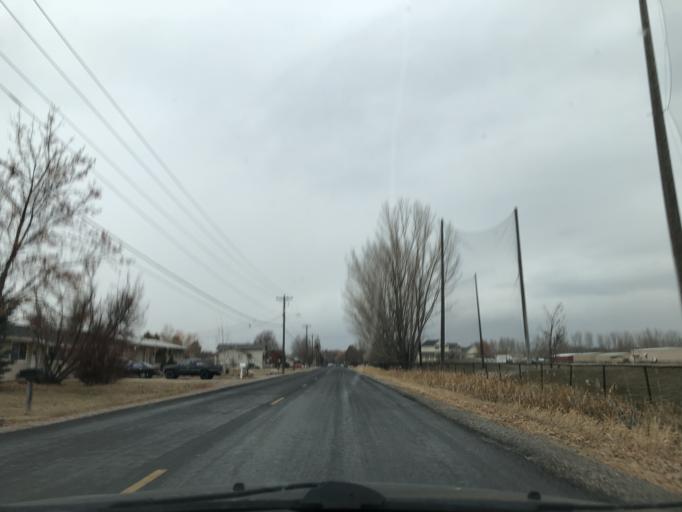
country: US
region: Utah
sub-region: Cache County
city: Logan
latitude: 41.7115
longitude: -111.8529
